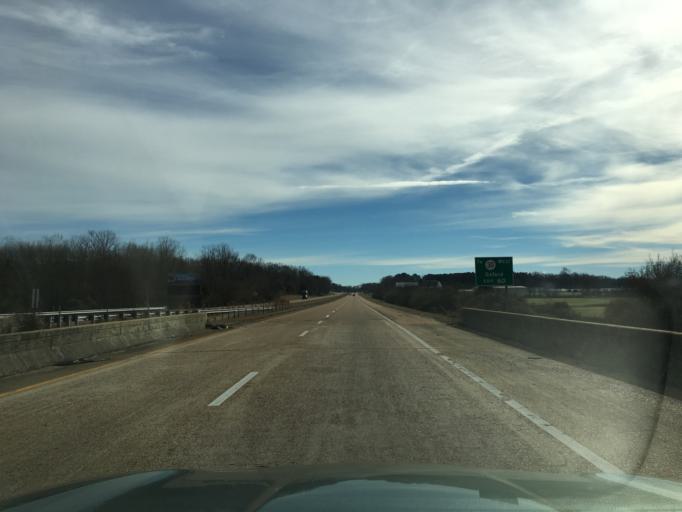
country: US
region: Mississippi
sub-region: Union County
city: New Albany
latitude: 34.5158
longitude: -89.0530
